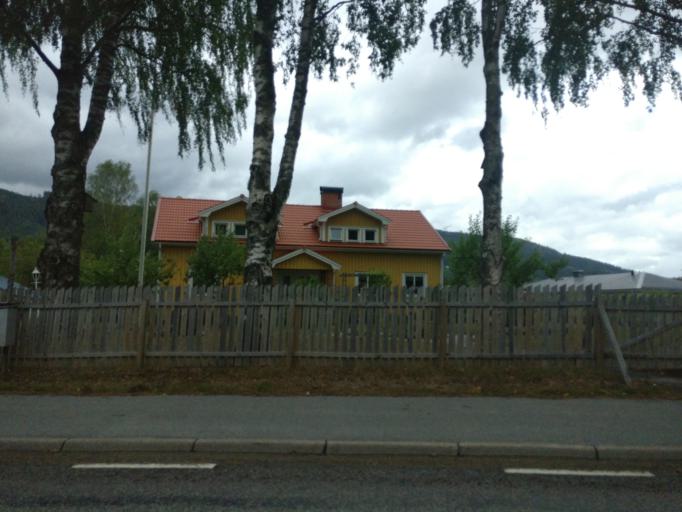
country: SE
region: Vaermland
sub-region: Torsby Kommun
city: Torsby
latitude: 60.7176
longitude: 12.8799
